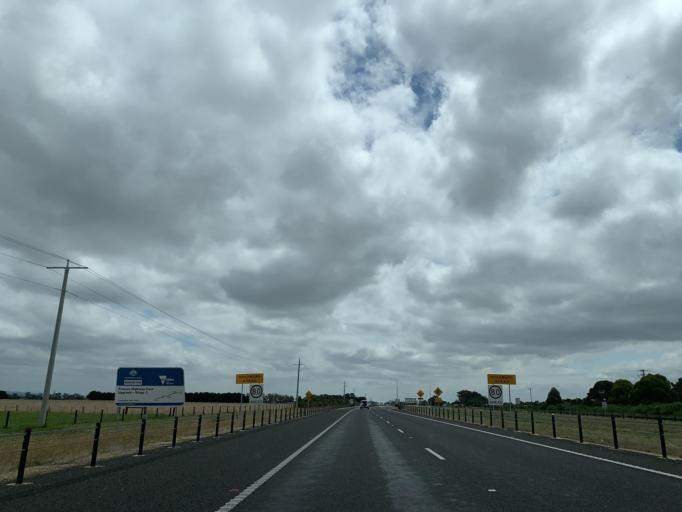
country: AU
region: Victoria
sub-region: Wellington
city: Sale
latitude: -38.1008
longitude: 146.9616
